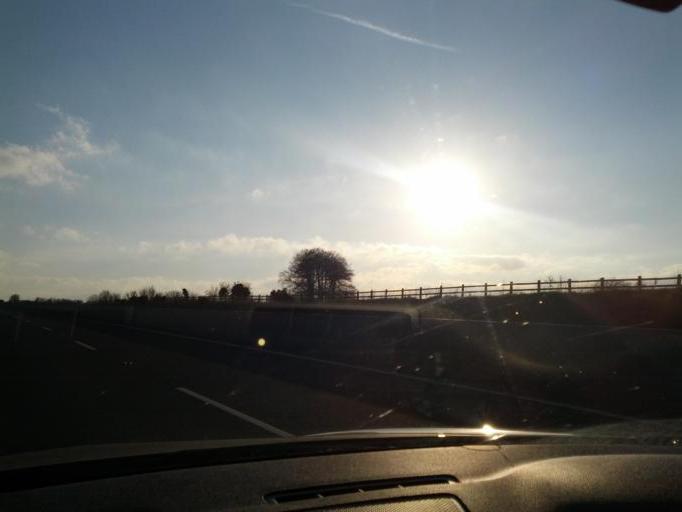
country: IE
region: Munster
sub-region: North Tipperary
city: Roscrea
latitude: 52.8981
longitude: -7.9063
